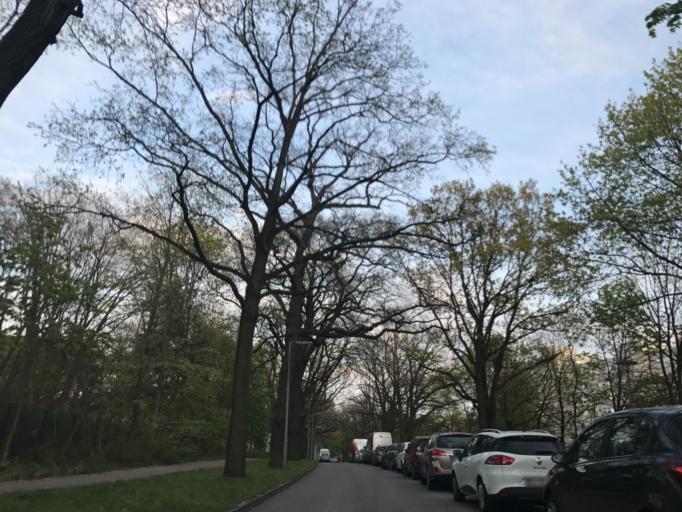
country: DE
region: Berlin
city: Haselhorst
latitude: 52.5096
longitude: 13.2241
